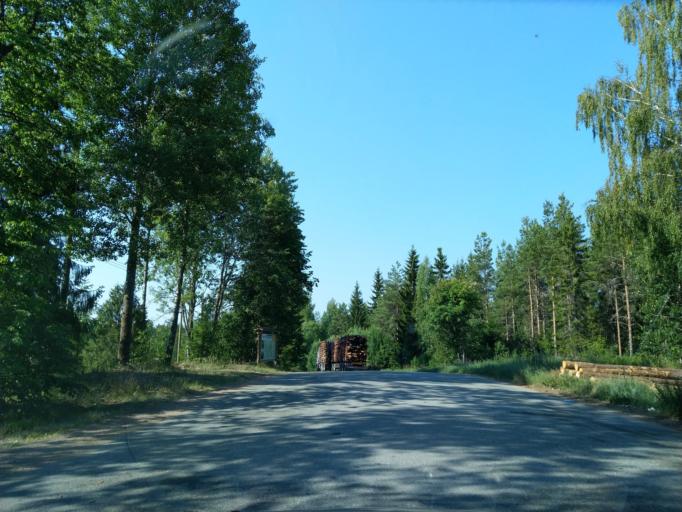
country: FI
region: Satakunta
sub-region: Pori
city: Pomarkku
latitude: 61.7201
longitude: 22.0518
